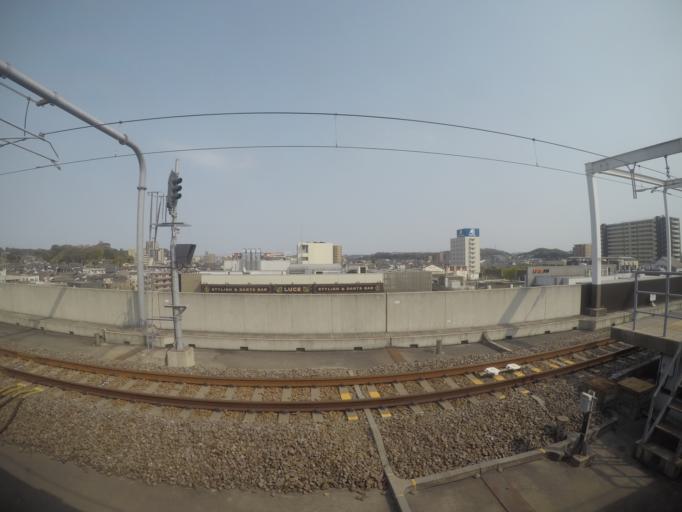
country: JP
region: Aichi
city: Obu
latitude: 35.0210
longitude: 136.8930
